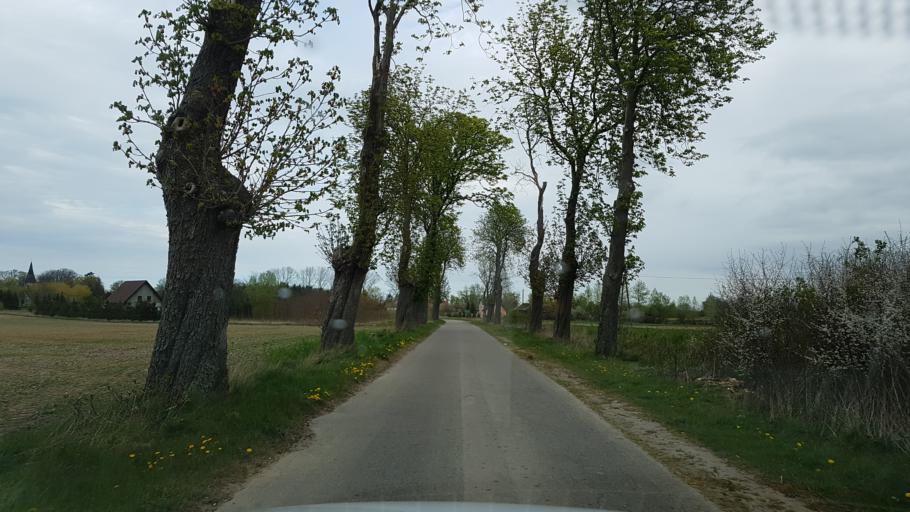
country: PL
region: West Pomeranian Voivodeship
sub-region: Powiat slawienski
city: Slawno
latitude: 54.5146
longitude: 16.6053
